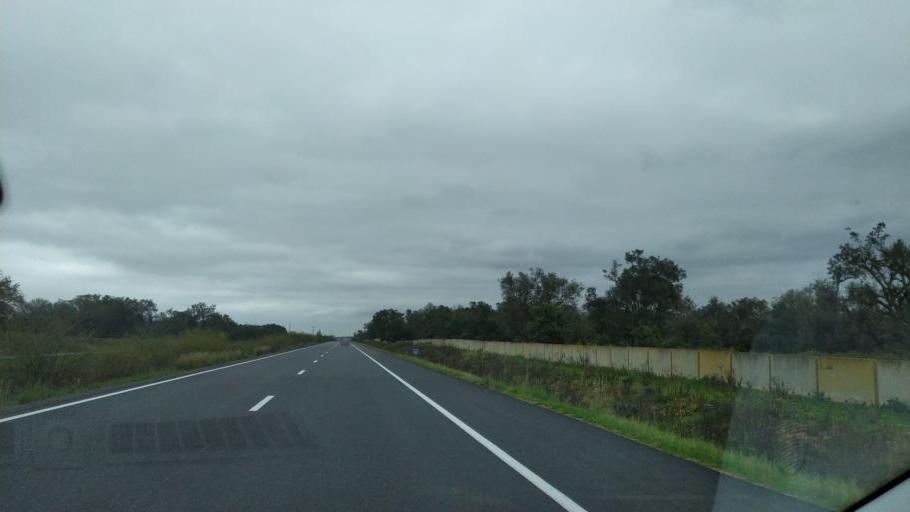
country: MA
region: Gharb-Chrarda-Beni Hssen
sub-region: Kenitra Province
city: Kenitra
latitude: 34.1808
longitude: -6.6501
